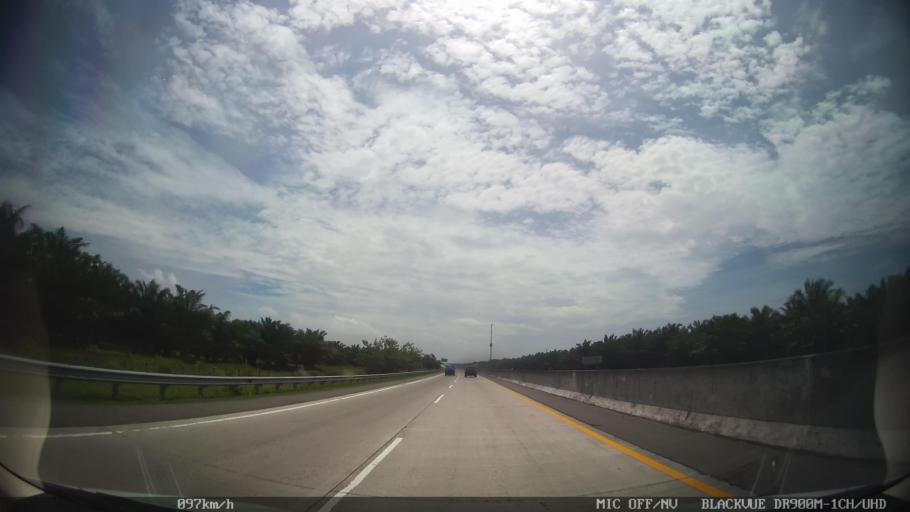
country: ID
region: North Sumatra
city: Perbaungan
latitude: 3.5318
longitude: 98.8774
